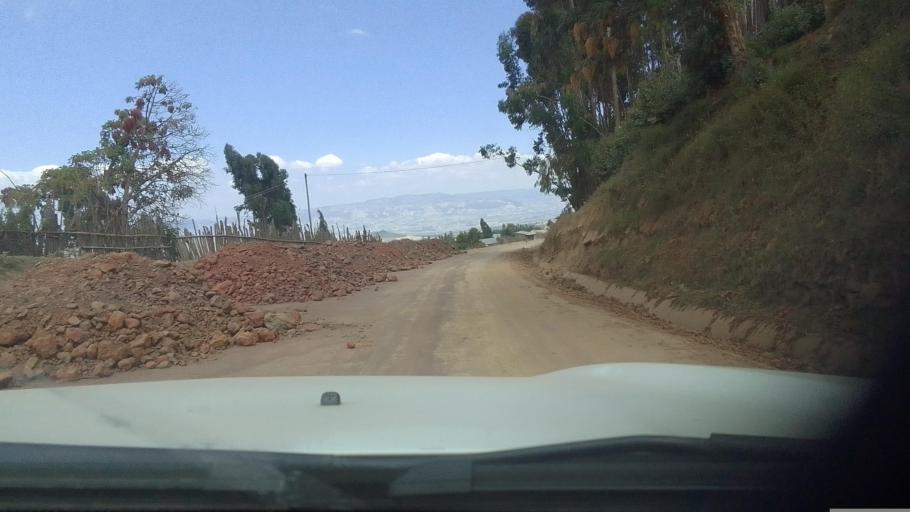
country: ET
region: Oromiya
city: Hagere Hiywet
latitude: 8.8430
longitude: 37.8853
